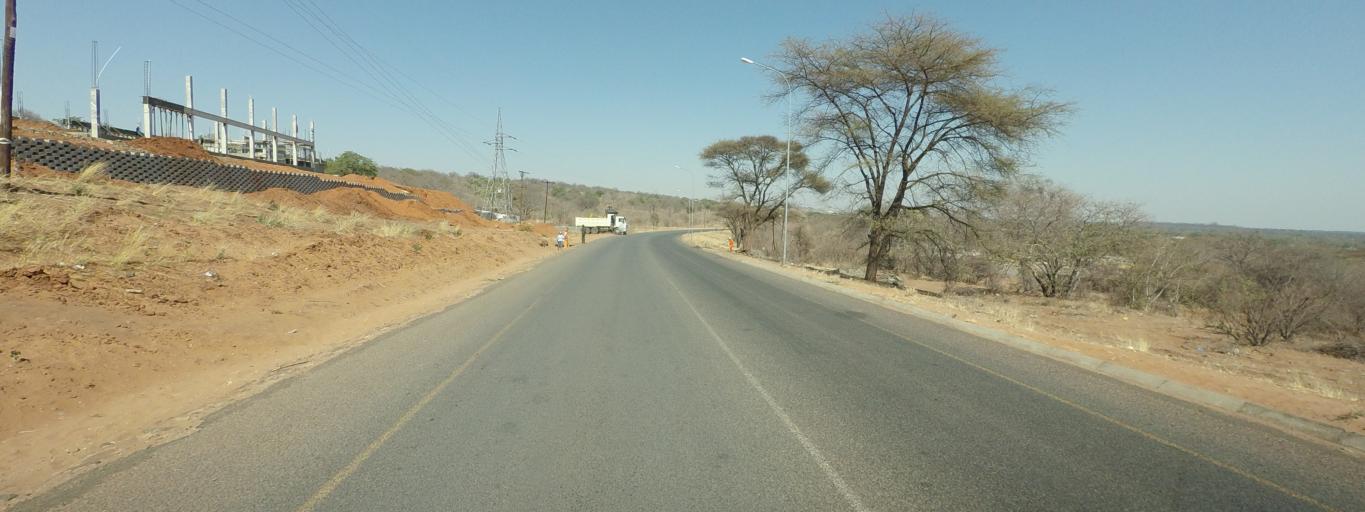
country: BW
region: North West
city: Kasane
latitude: -17.7998
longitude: 25.2250
